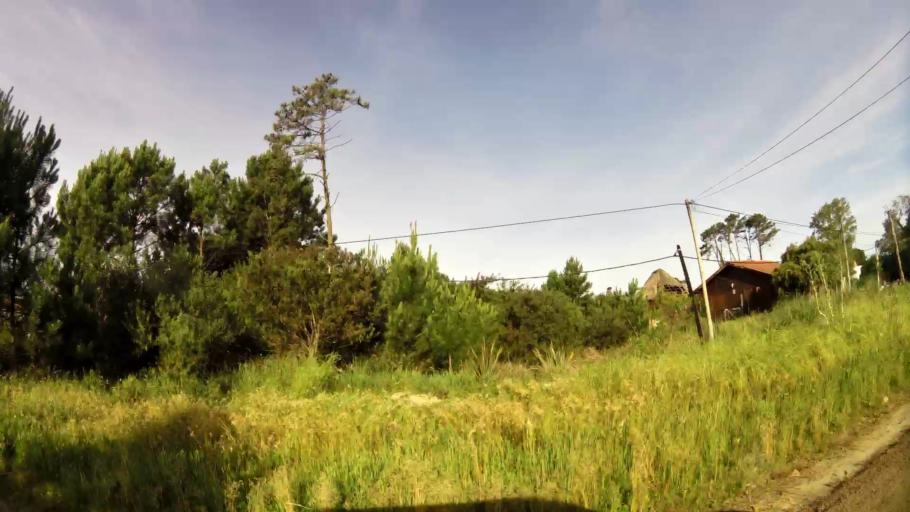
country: UY
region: Canelones
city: Empalme Olmos
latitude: -34.7843
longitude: -55.8588
